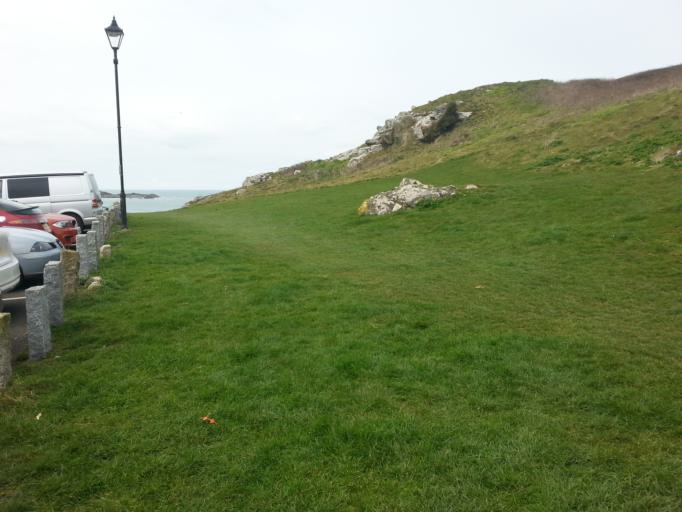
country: GB
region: England
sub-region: Cornwall
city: St Ives
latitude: 50.2172
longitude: -5.4779
